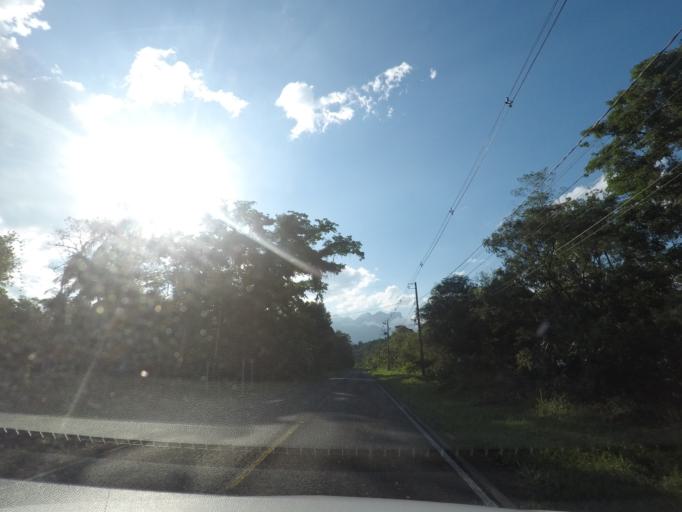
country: BR
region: Parana
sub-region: Antonina
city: Antonina
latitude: -25.4309
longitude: -48.8738
